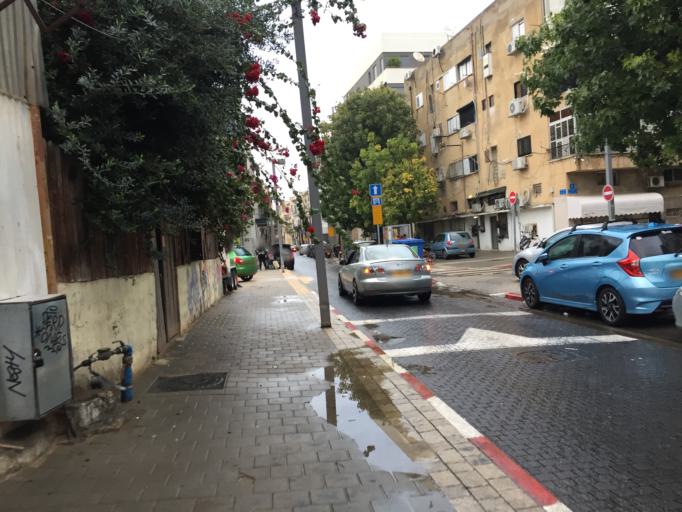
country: IL
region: Tel Aviv
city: Yafo
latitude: 32.0522
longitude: 34.7584
